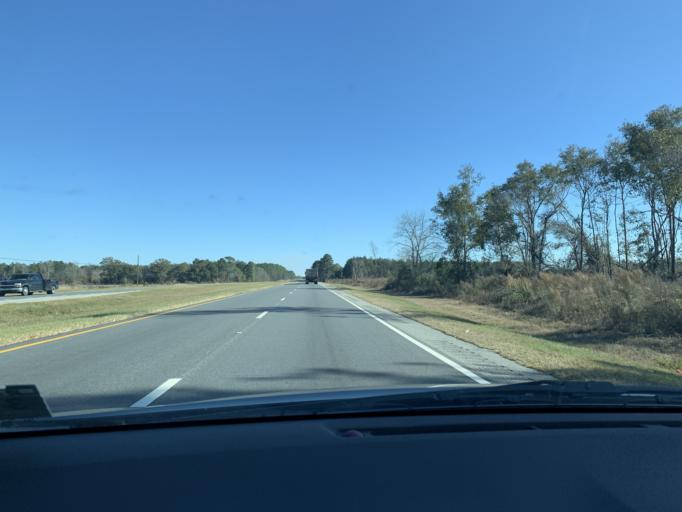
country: US
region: Georgia
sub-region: Atkinson County
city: Willacoochee
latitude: 31.3324
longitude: -83.0183
